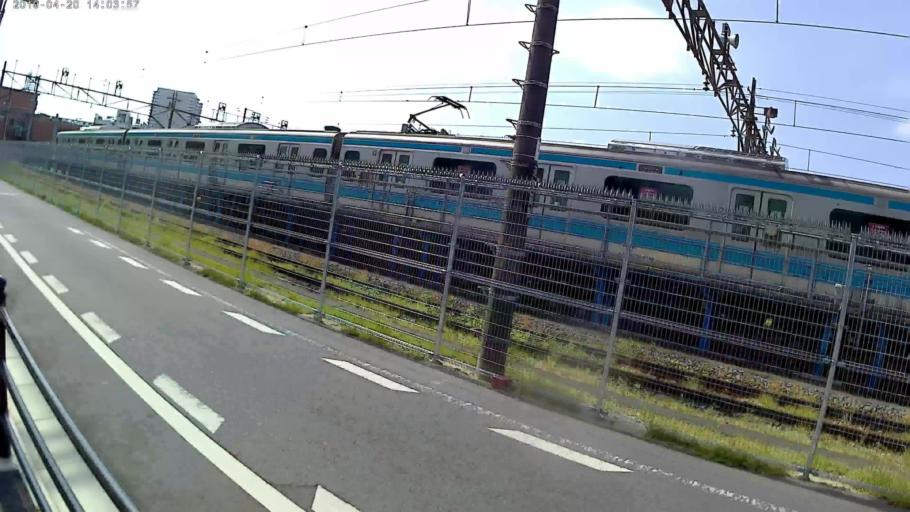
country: JP
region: Kanagawa
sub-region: Kawasaki-shi
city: Kawasaki
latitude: 35.5557
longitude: 139.7101
